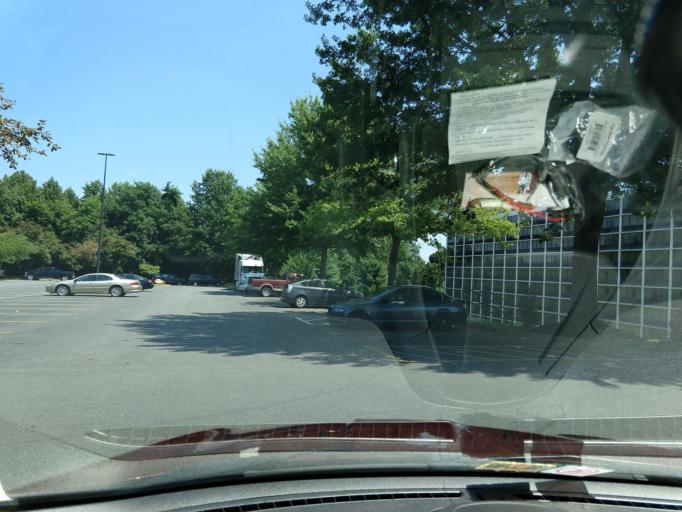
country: US
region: Virginia
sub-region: Albemarle County
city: Hollymead
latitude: 38.1005
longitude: -78.4652
